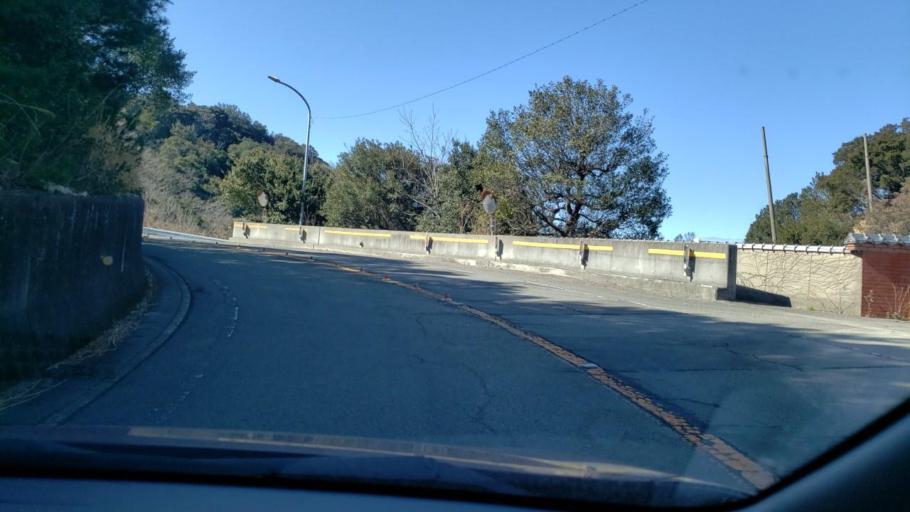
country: JP
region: Tokushima
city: Narutocho-mitsuishi
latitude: 34.2389
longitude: 134.6078
